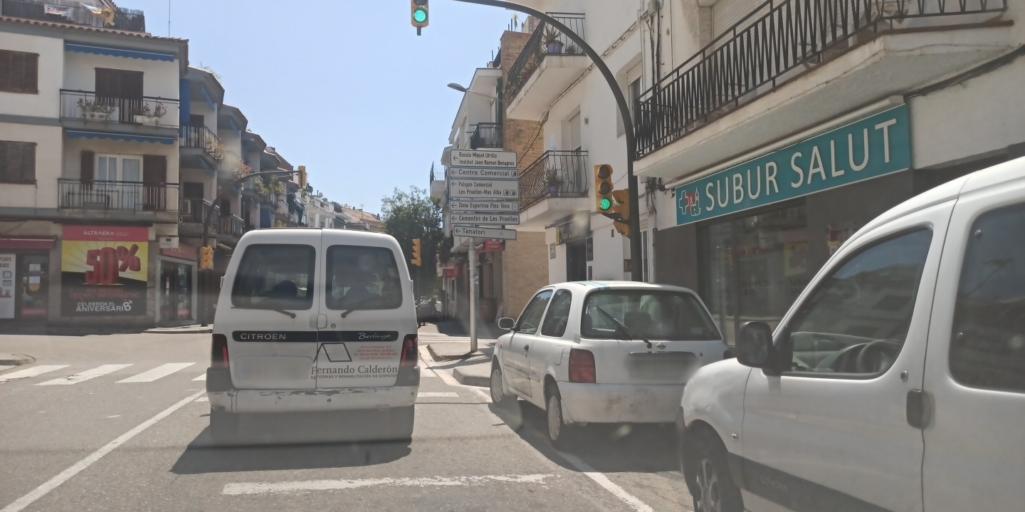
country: ES
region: Catalonia
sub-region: Provincia de Barcelona
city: Sitges
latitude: 41.2402
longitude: 1.8101
